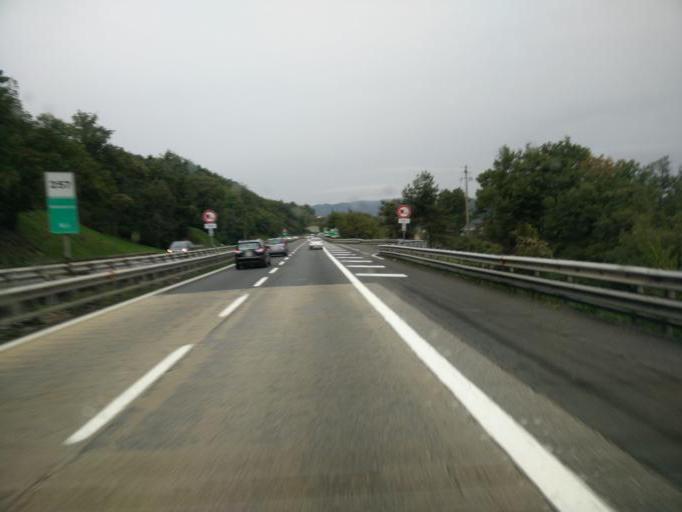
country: IT
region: Tuscany
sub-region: Province of Florence
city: Barberino di Mugello
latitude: 44.0197
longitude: 11.2243
